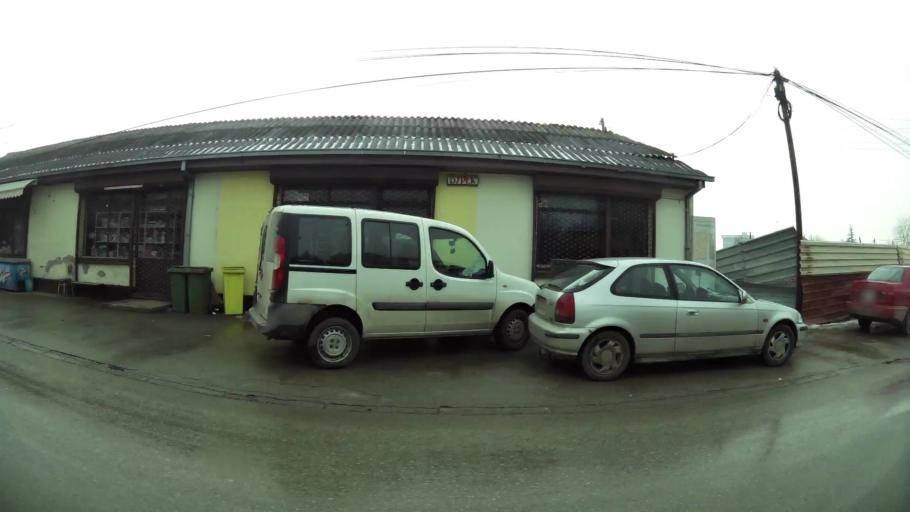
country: MK
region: Ilinden
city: Ilinden
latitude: 41.9958
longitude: 21.5703
